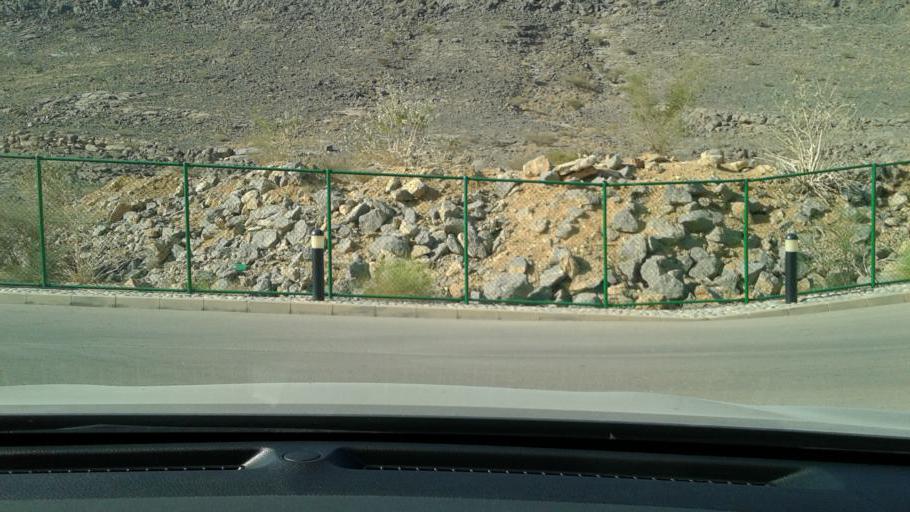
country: OM
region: Muhafazat ad Dakhiliyah
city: Bahla'
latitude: 23.0814
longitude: 57.3497
